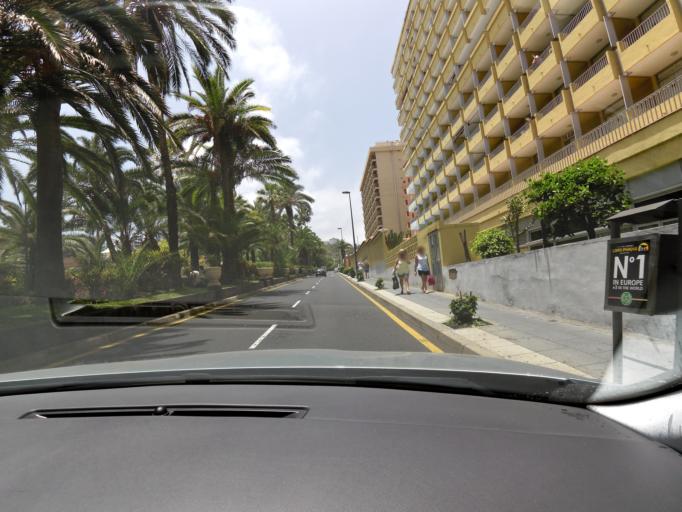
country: ES
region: Canary Islands
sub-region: Provincia de Santa Cruz de Tenerife
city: Puerto de la Cruz
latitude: 28.4170
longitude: -16.5422
